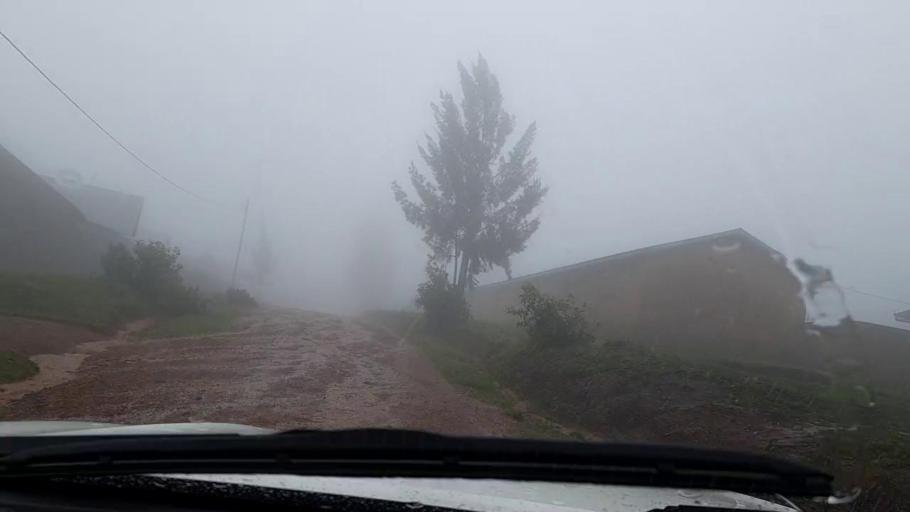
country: RW
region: Northern Province
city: Byumba
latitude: -1.7331
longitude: 30.0250
